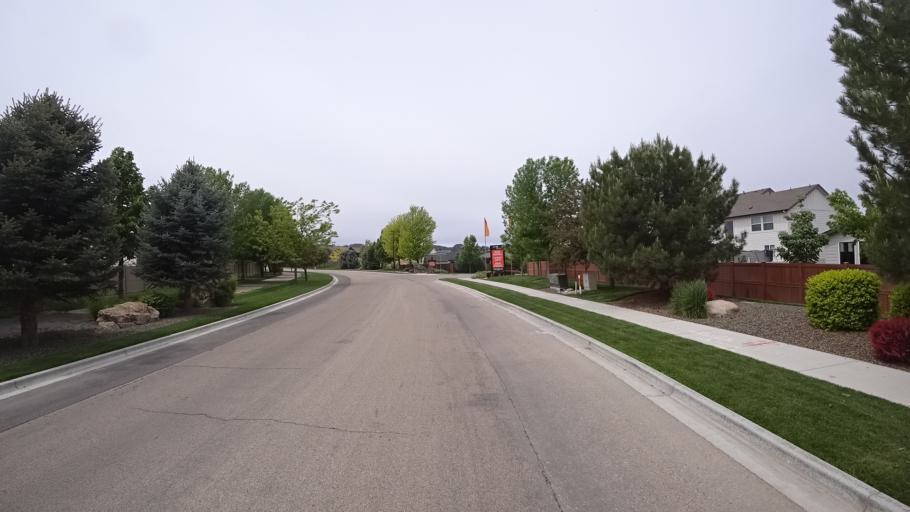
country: US
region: Idaho
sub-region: Ada County
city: Meridian
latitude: 43.5538
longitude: -116.3617
